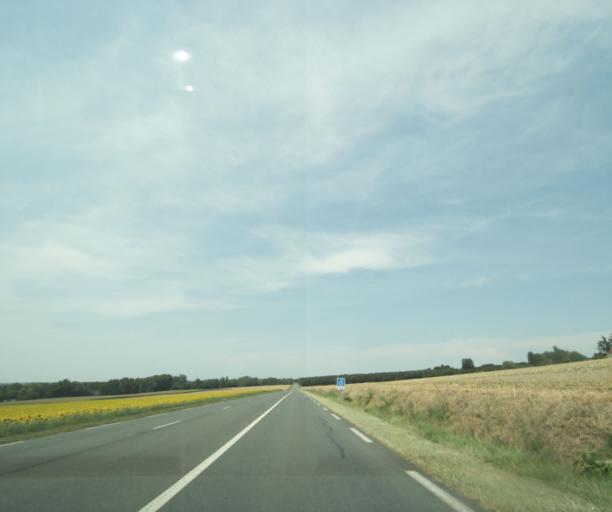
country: FR
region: Poitou-Charentes
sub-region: Departement de la Vienne
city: Vouneuil-sur-Vienne
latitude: 46.7398
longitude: 0.5539
